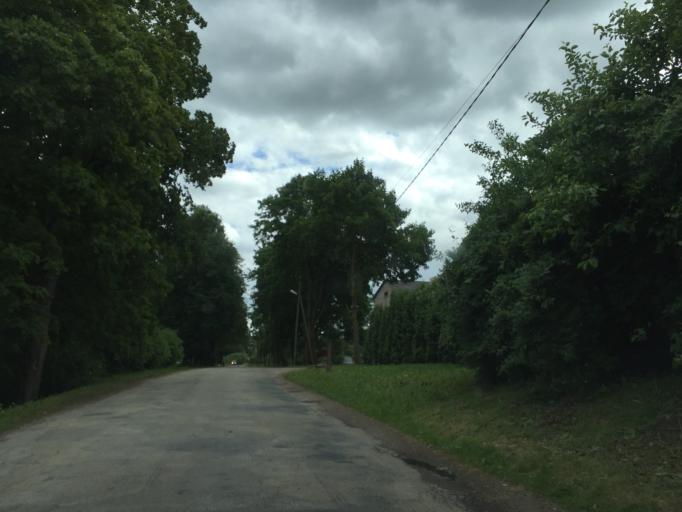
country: LV
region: Lecava
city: Iecava
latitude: 56.5924
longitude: 24.2087
